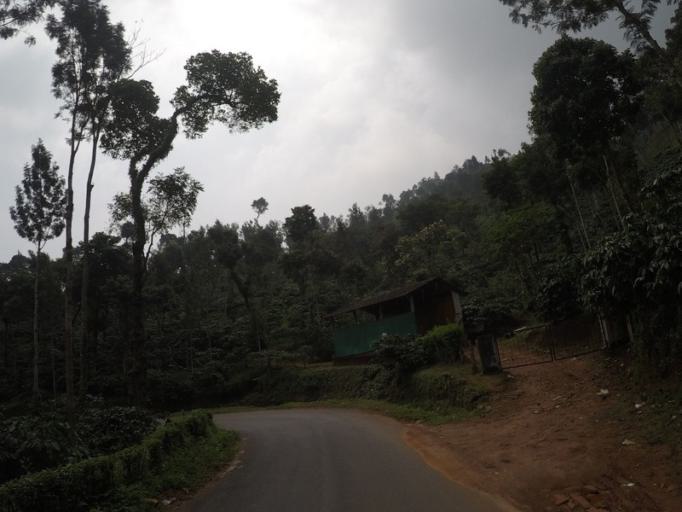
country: IN
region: Karnataka
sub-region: Chikmagalur
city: Mudigere
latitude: 13.1671
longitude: 75.4366
